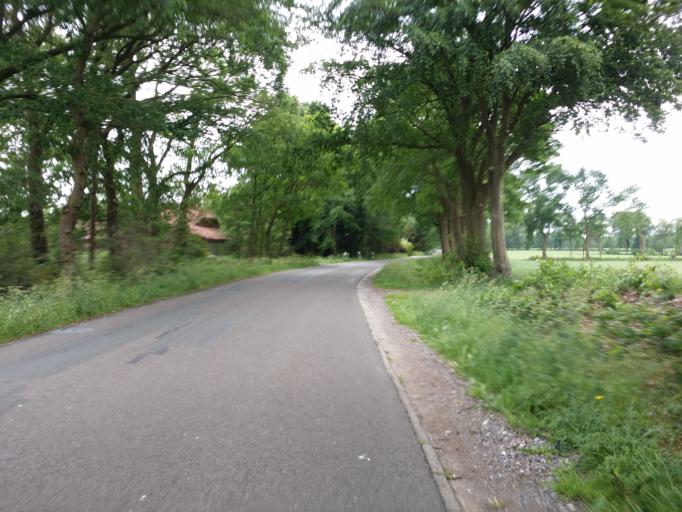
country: DE
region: Lower Saxony
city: Bockhorn
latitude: 53.3622
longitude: 8.0088
